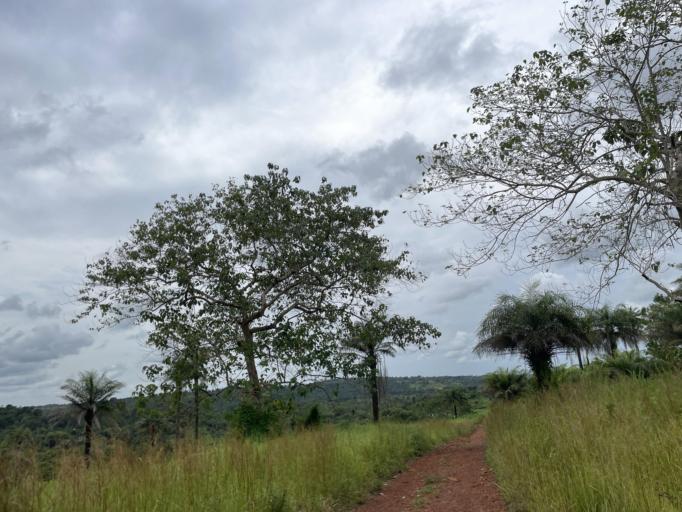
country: SL
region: Northern Province
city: Kambia
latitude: 9.1330
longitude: -12.9116
